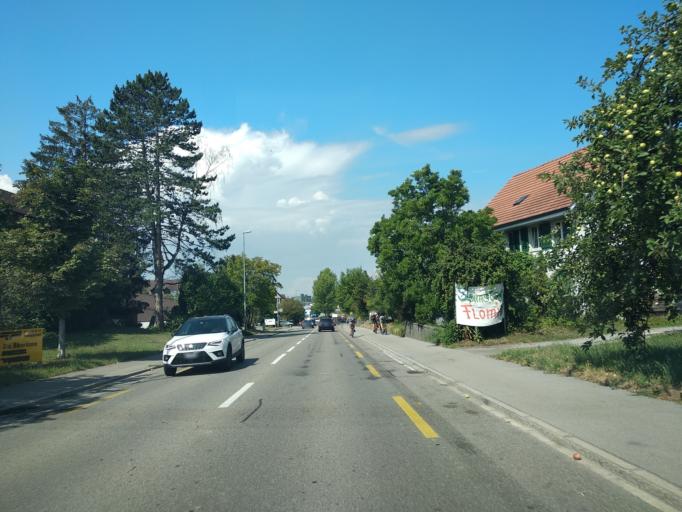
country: CH
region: Thurgau
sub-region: Frauenfeld District
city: Frauenfeld
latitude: 47.5639
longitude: 8.8739
